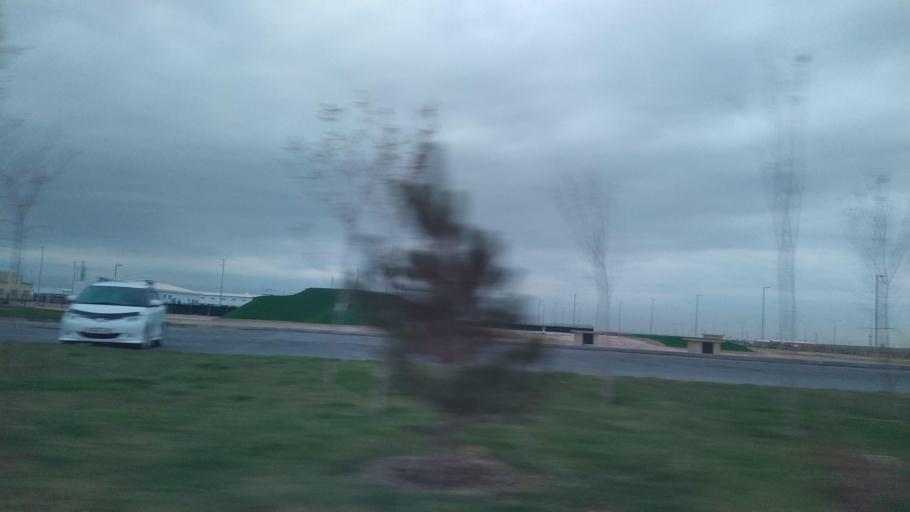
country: KZ
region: Ongtustik Qazaqstan
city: Kentau
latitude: 43.3168
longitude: 68.5456
